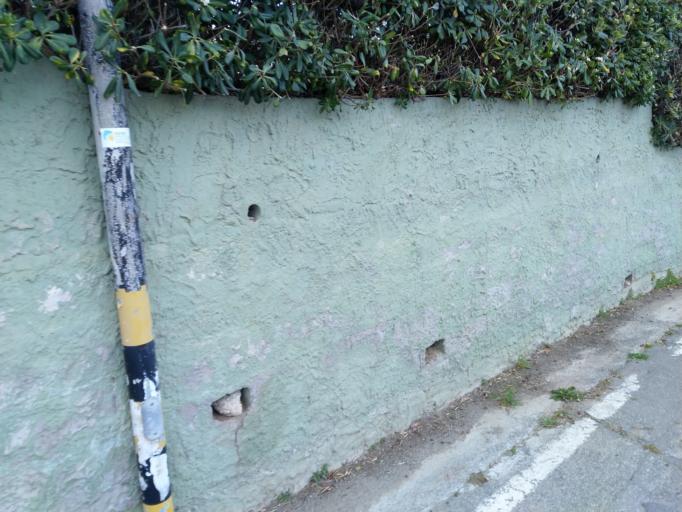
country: IT
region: Sardinia
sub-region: Provincia di Cagliari
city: Olia Speciosa
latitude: 39.2544
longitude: 9.5699
